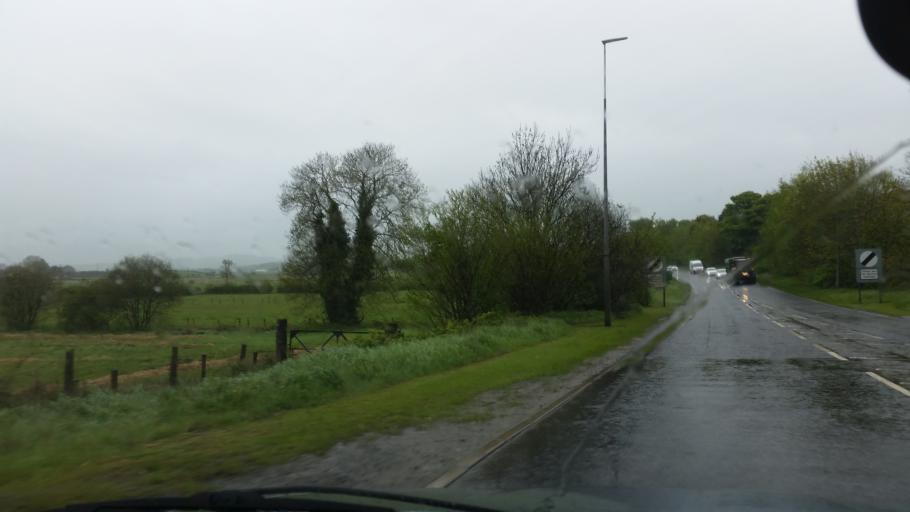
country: GB
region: Northern Ireland
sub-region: Strabane District
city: Strabane
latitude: 54.8425
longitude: -7.4503
